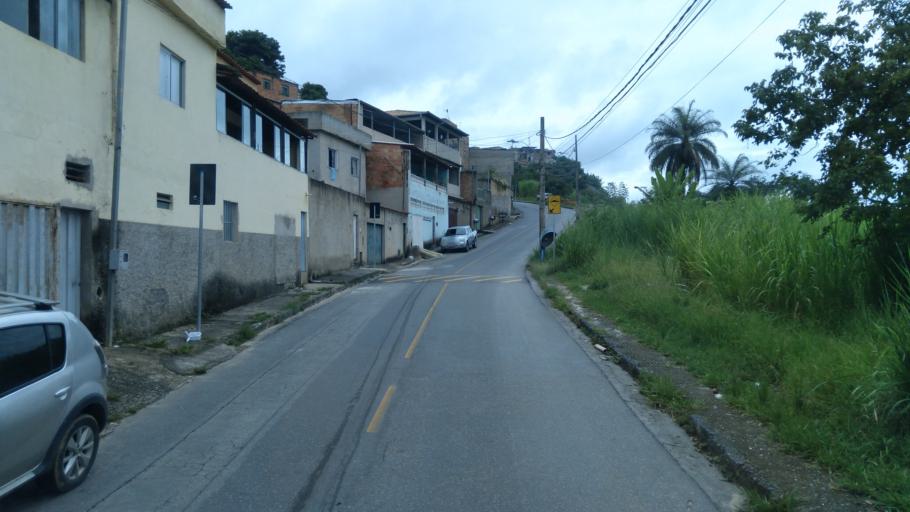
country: BR
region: Minas Gerais
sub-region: Santa Luzia
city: Santa Luzia
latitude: -19.8323
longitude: -43.8671
